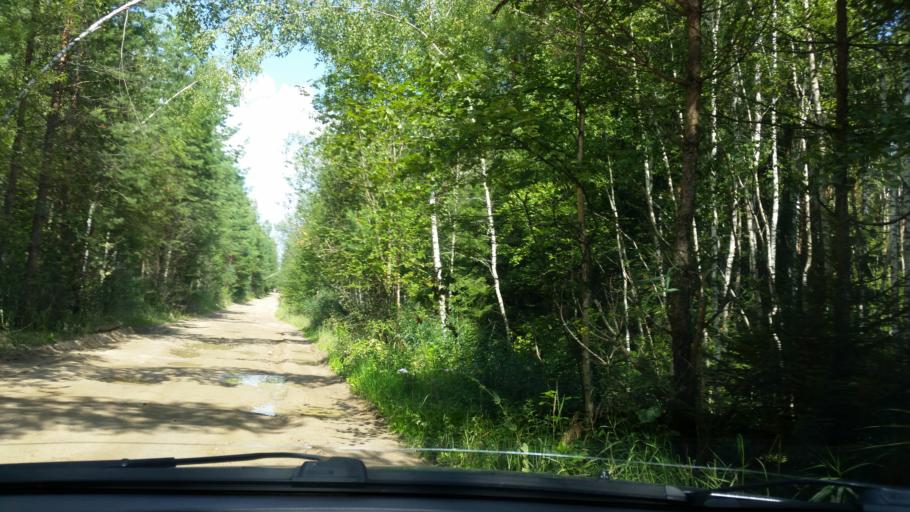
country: RU
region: Moskovskaya
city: Pushchino
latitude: 54.9107
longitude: 37.6856
